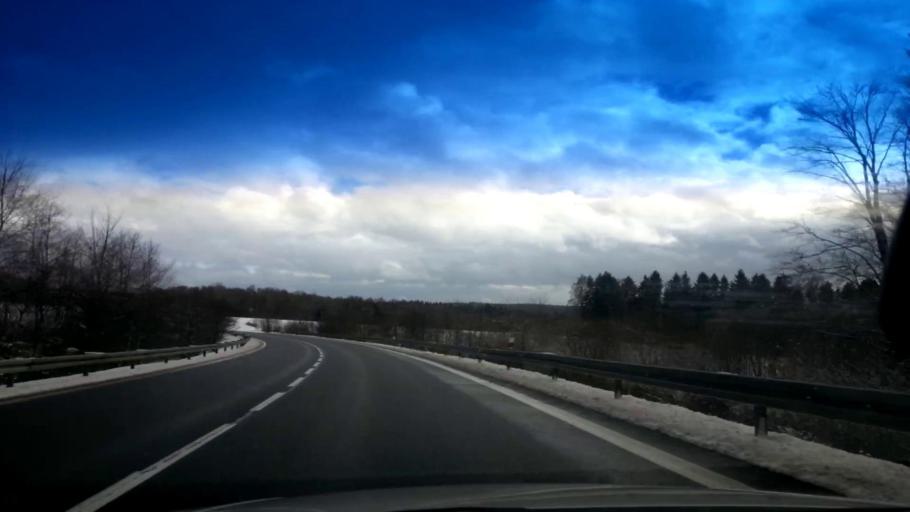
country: CZ
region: Karlovarsky
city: As
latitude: 50.2096
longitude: 12.1819
